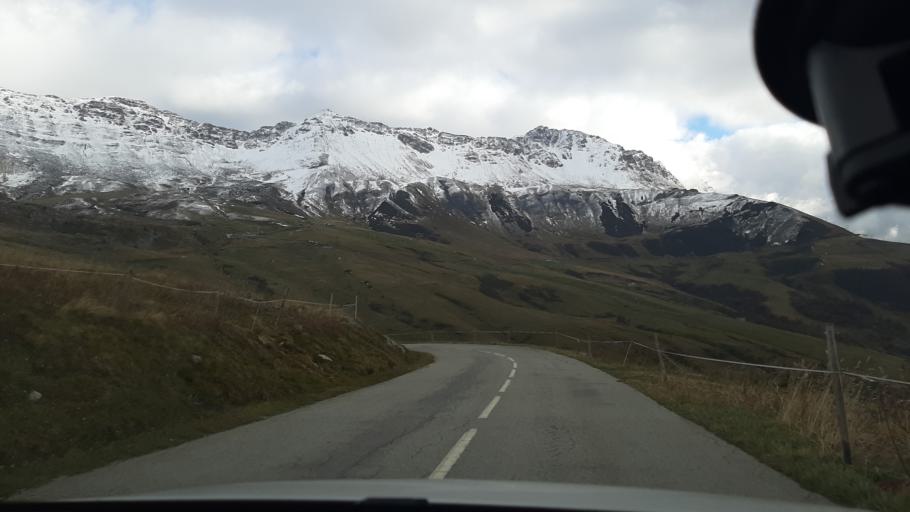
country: FR
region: Rhone-Alpes
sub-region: Departement de la Savoie
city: La Chambre
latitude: 45.4279
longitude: 6.3679
